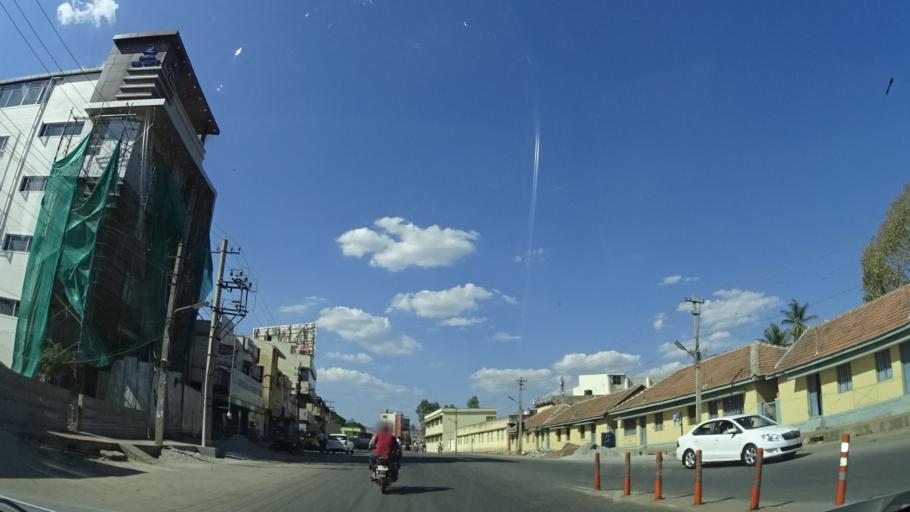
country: IN
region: Karnataka
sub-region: Chikmagalur
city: Chikmagalur
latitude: 13.3135
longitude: 75.7711
